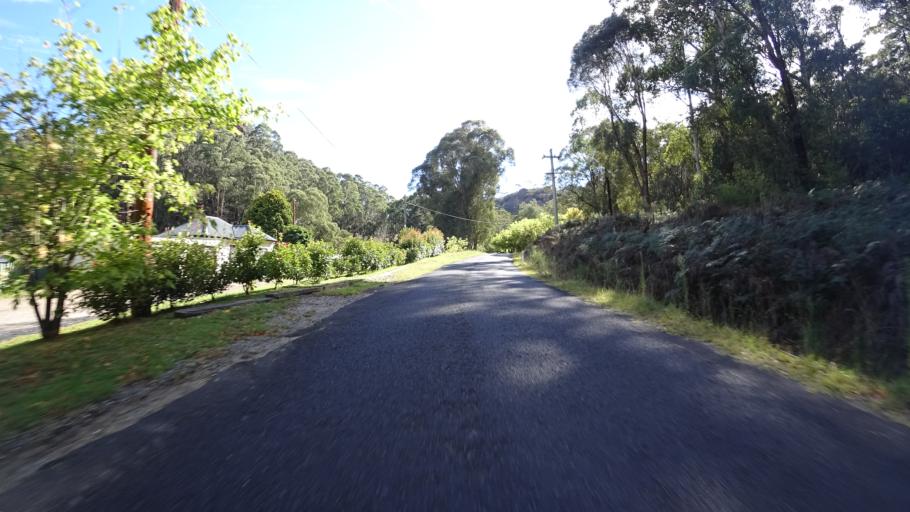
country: AU
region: New South Wales
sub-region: Lithgow
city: Lithgow
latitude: -33.4564
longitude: 150.1724
